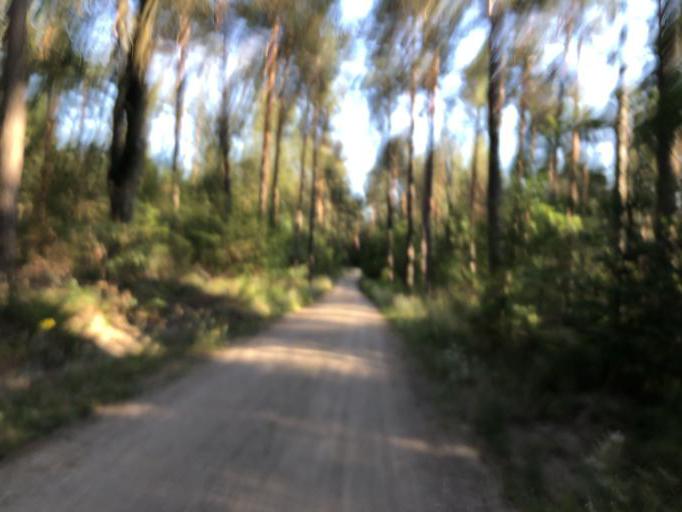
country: DE
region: Bavaria
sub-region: Regierungsbezirk Mittelfranken
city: Uttenreuth
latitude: 49.5556
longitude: 11.0780
